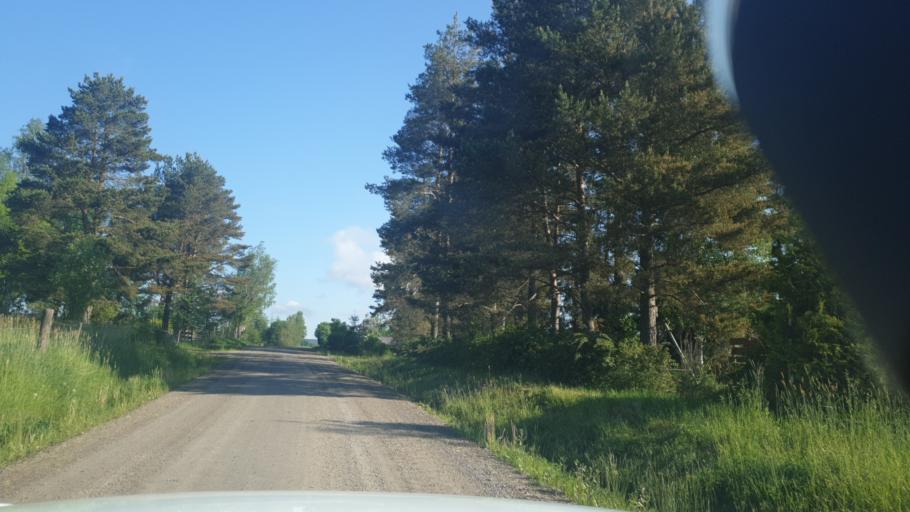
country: SE
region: Vaermland
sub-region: Eda Kommun
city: Charlottenberg
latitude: 59.7249
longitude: 12.1447
